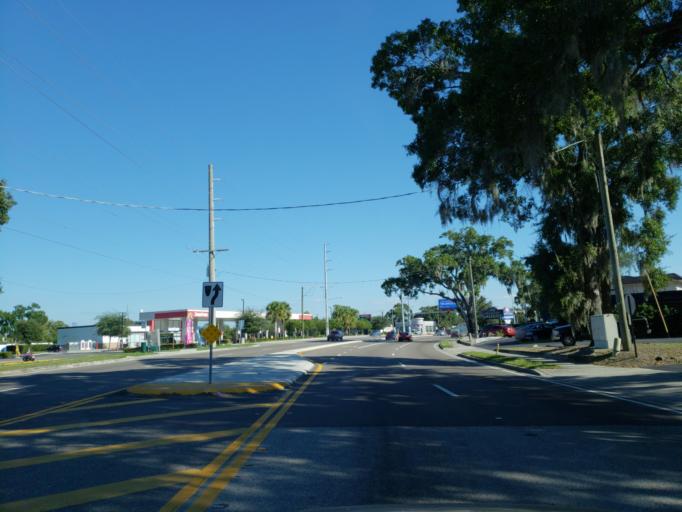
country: US
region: Florida
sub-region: Hillsborough County
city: Carrollwood
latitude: 28.0413
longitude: -82.5100
